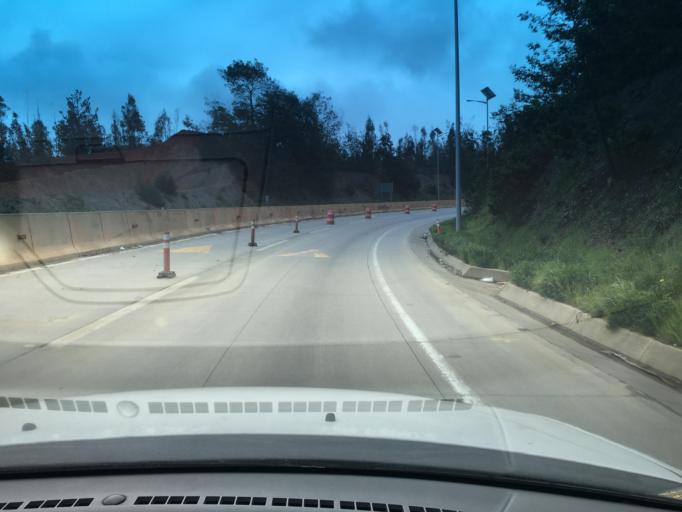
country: CL
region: Valparaiso
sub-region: Provincia de Valparaiso
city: Valparaiso
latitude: -33.0894
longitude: -71.6147
